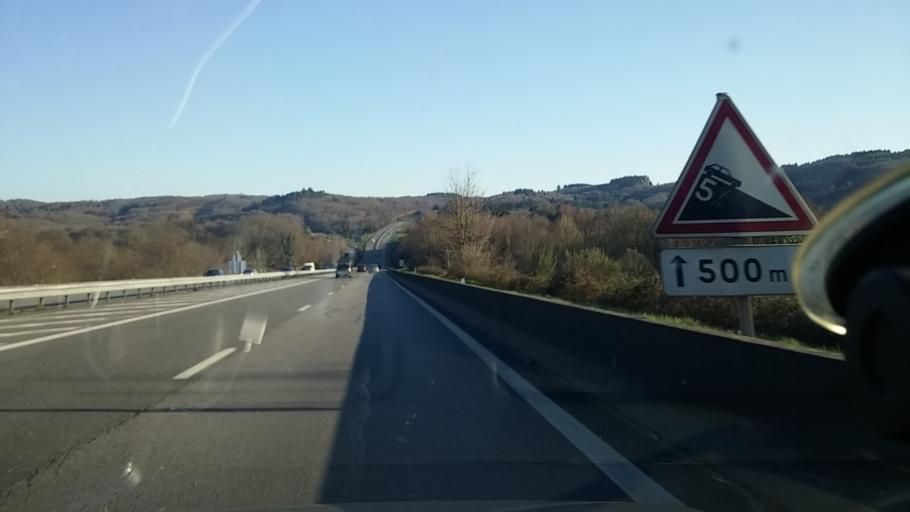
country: FR
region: Limousin
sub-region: Departement de la Haute-Vienne
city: Bessines-sur-Gartempe
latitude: 46.0788
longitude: 1.3572
